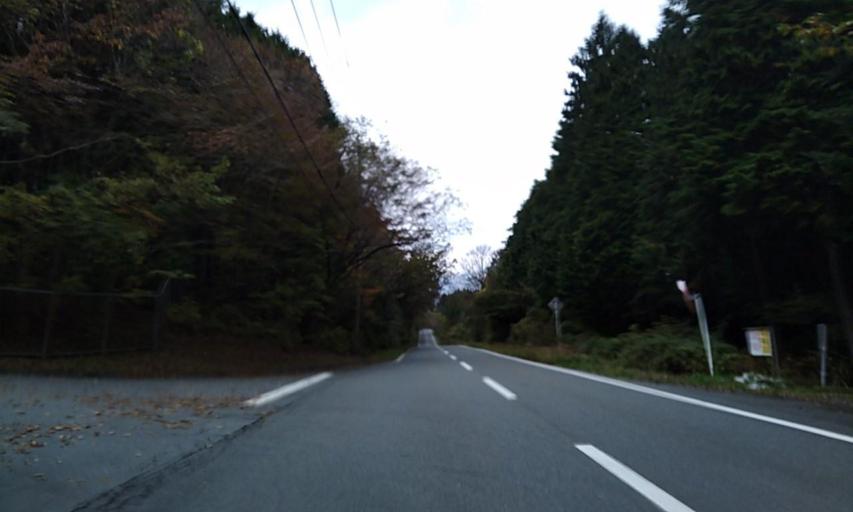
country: JP
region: Shizuoka
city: Gotemba
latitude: 35.2618
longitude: 138.8098
